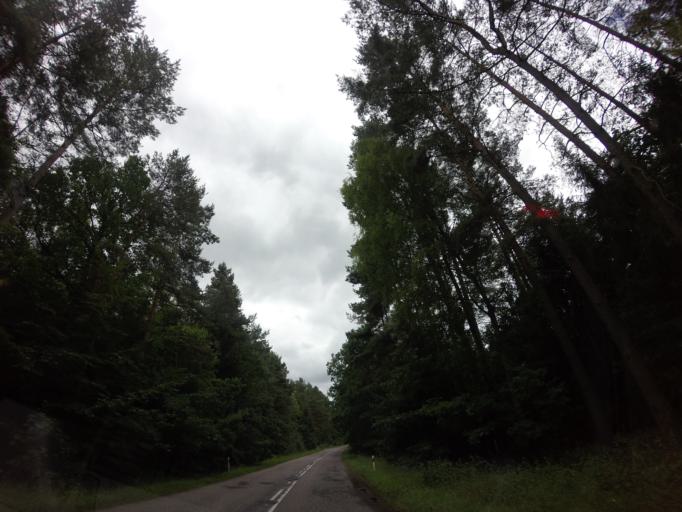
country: PL
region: West Pomeranian Voivodeship
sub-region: Powiat stargardzki
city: Insko
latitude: 53.3510
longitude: 15.5911
